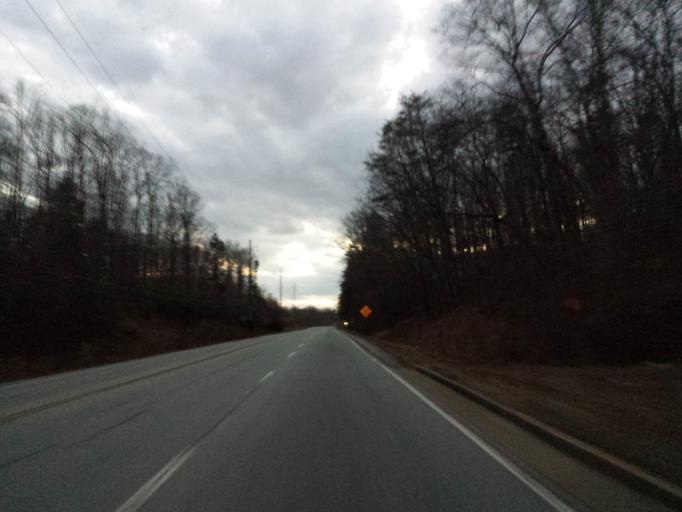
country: US
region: Georgia
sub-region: White County
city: Cleveland
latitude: 34.6526
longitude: -83.7319
